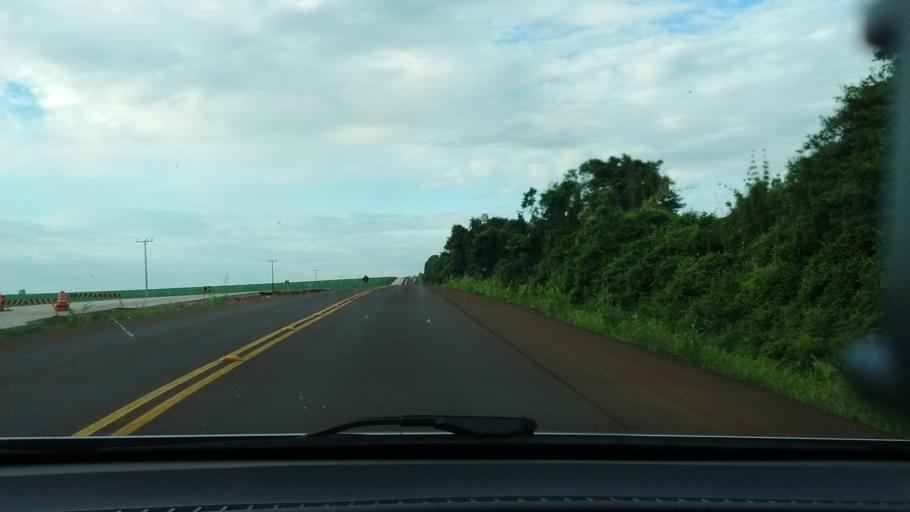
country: BR
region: Parana
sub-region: Cascavel
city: Cascavel
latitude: -25.0448
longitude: -53.5567
